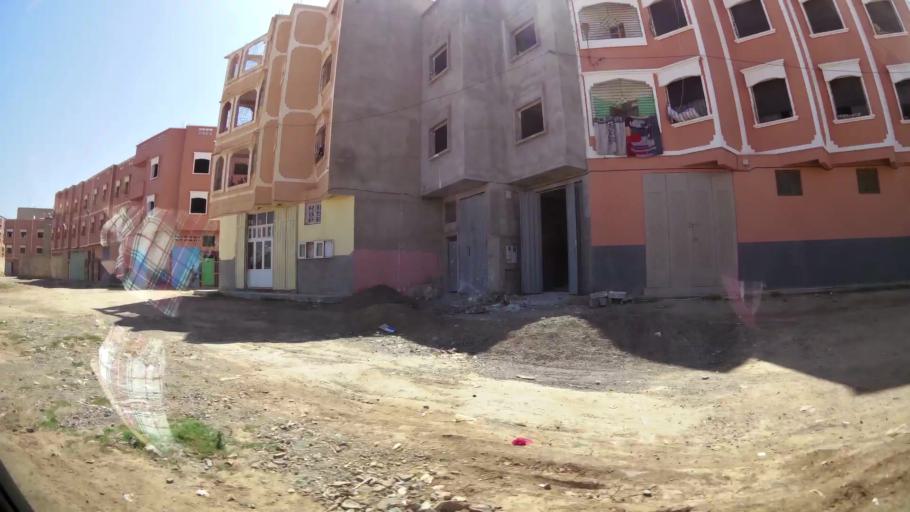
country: MA
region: Souss-Massa-Draa
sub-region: Inezgane-Ait Mellou
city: Inezgane
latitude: 30.3382
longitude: -9.5079
